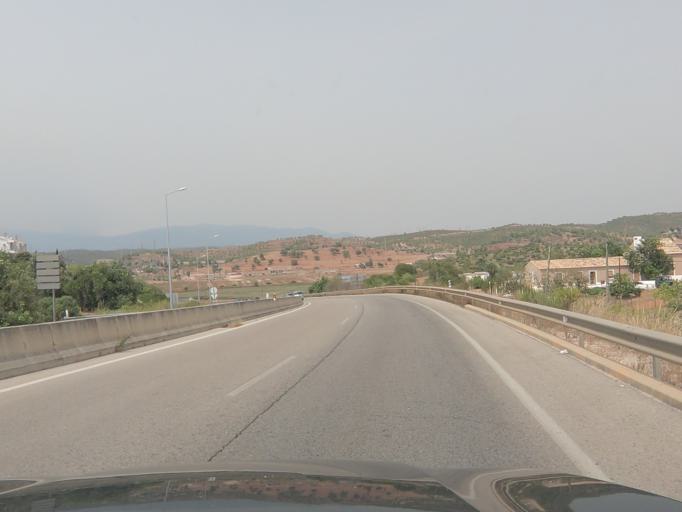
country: PT
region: Faro
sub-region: Portimao
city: Portimao
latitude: 37.1673
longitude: -8.5310
